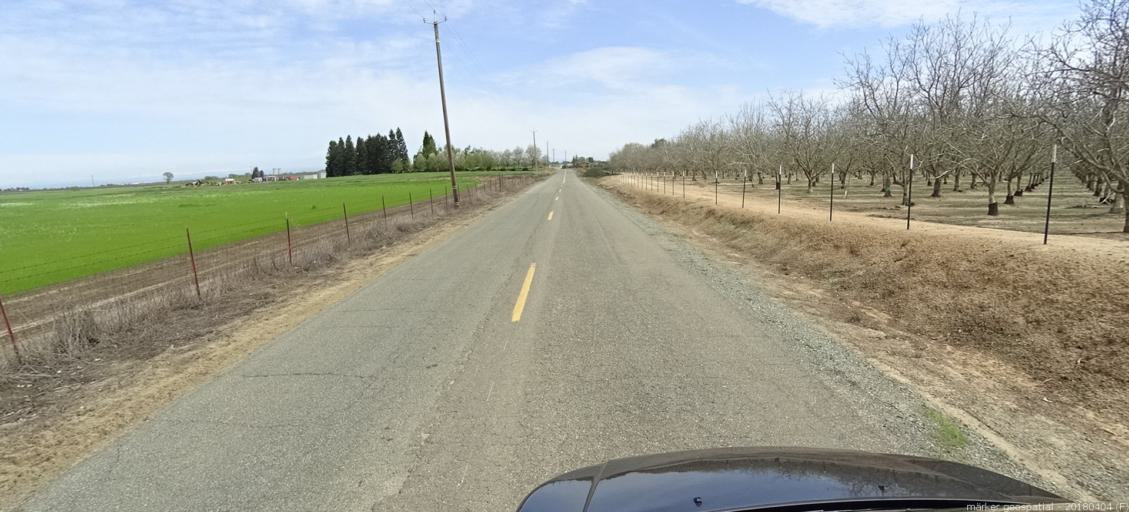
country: US
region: California
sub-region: Sacramento County
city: Herald
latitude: 38.3068
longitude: -121.2122
